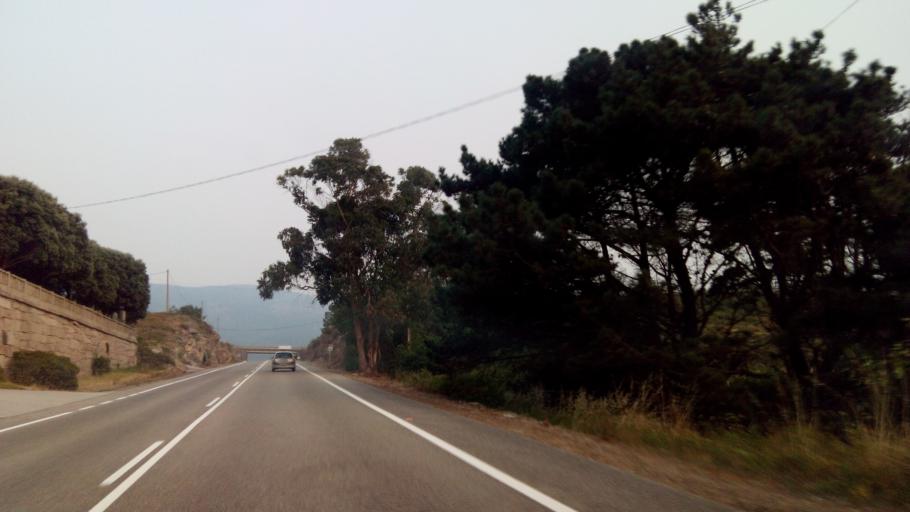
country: ES
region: Galicia
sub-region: Provincia de Pontevedra
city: Oia
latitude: 42.0559
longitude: -8.8870
